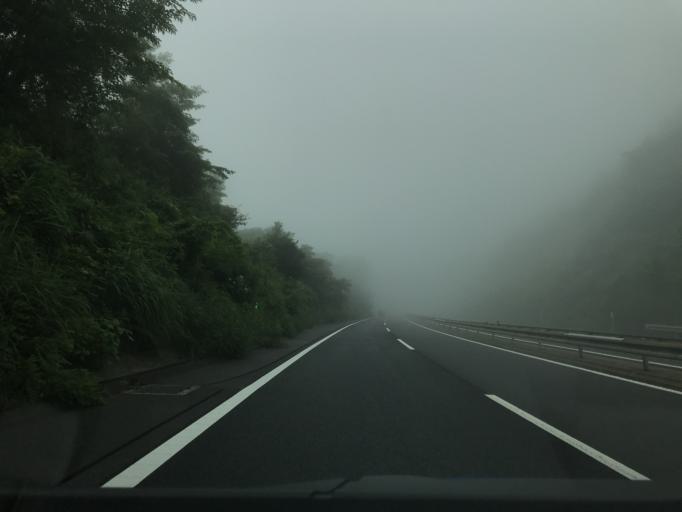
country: JP
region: Oita
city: Hiji
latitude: 33.3675
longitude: 131.4553
